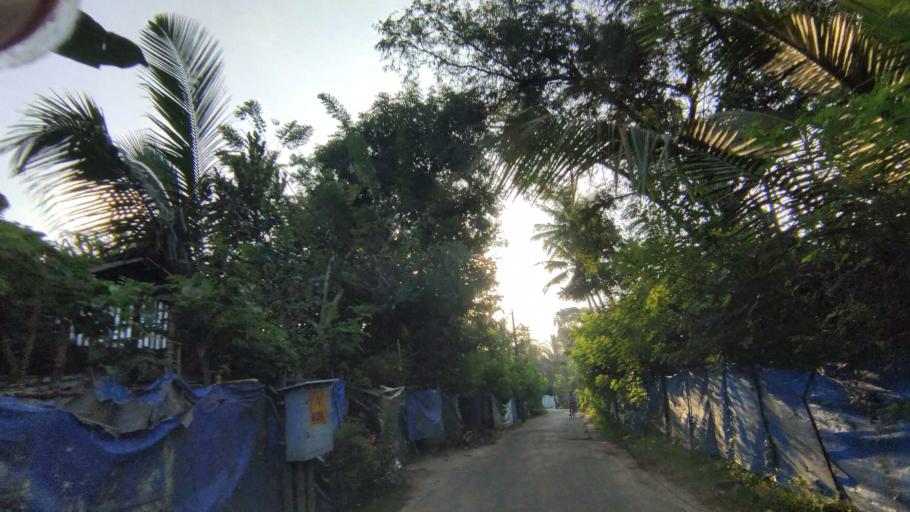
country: IN
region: Kerala
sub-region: Alappuzha
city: Shertallai
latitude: 9.6475
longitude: 76.3688
